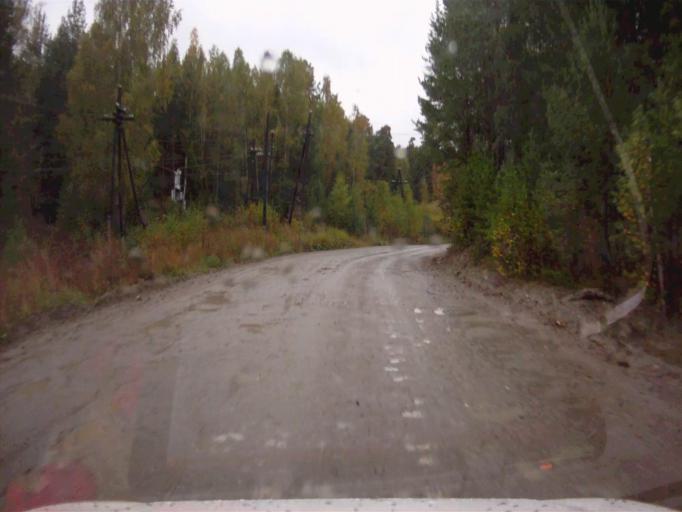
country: RU
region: Chelyabinsk
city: Kyshtym
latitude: 55.7437
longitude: 60.4931
